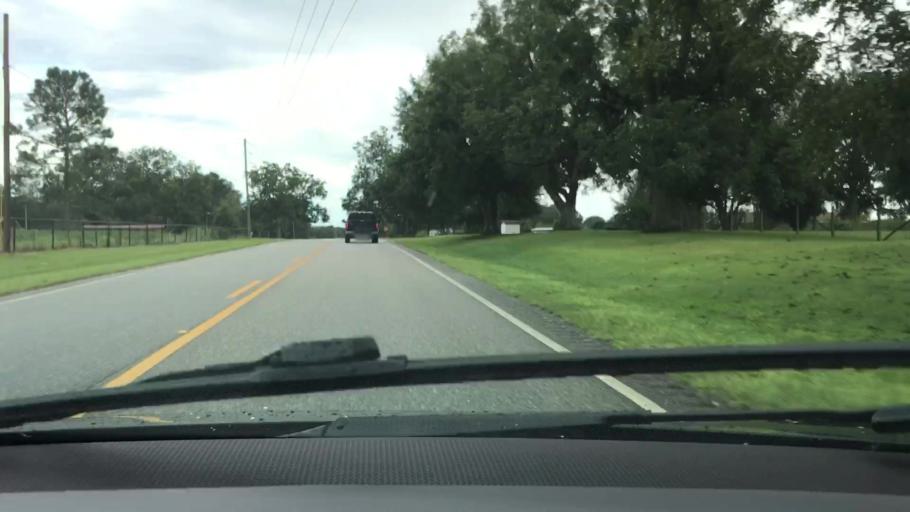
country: US
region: Alabama
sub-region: Geneva County
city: Samson
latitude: 31.0882
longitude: -86.1088
